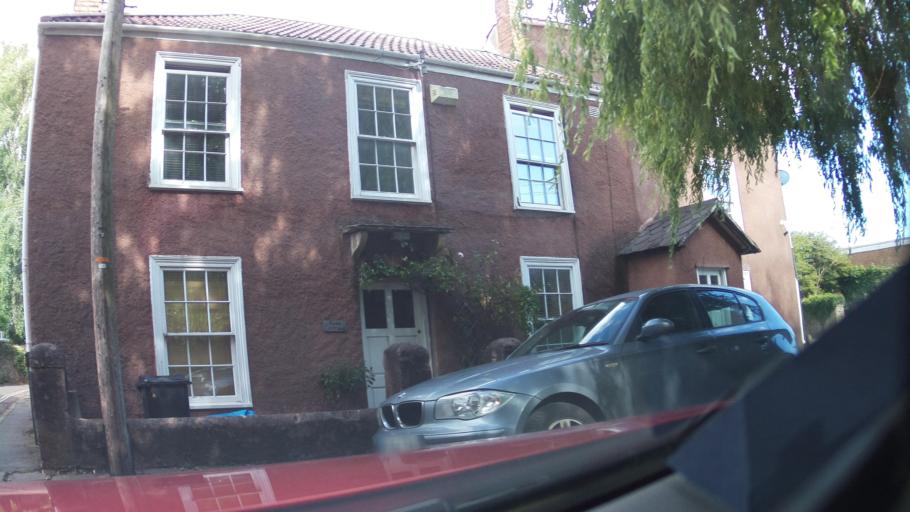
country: GB
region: England
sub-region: South Gloucestershire
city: Stoke Gifford
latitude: 51.4814
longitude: -2.5545
